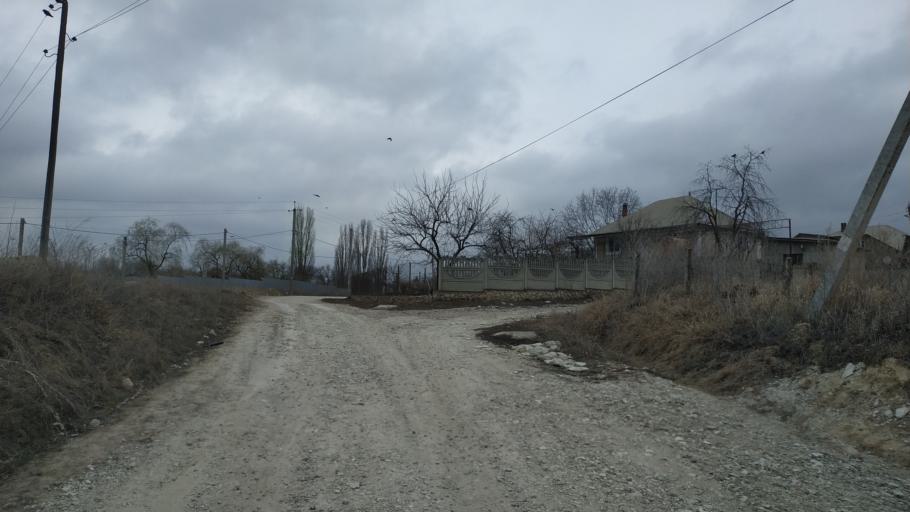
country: MD
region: Laloveni
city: Ialoveni
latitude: 46.9328
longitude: 28.7948
